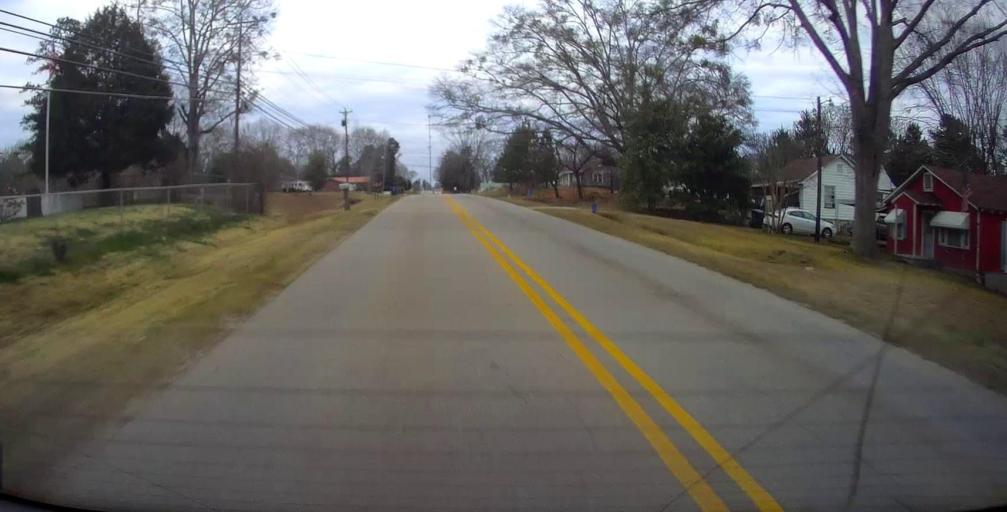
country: US
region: Alabama
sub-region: Chambers County
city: Huguley
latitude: 32.8408
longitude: -85.2327
